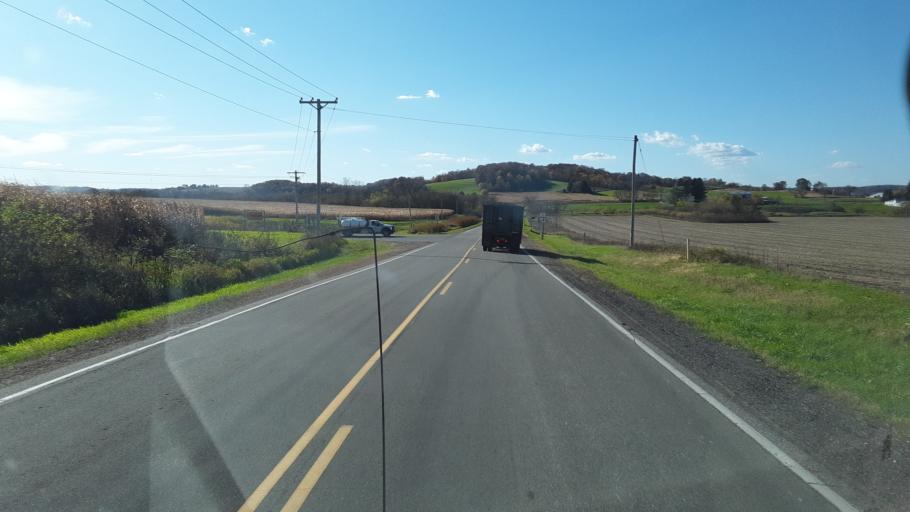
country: US
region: Wisconsin
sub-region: Sauk County
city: Reedsburg
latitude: 43.5405
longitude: -90.1629
